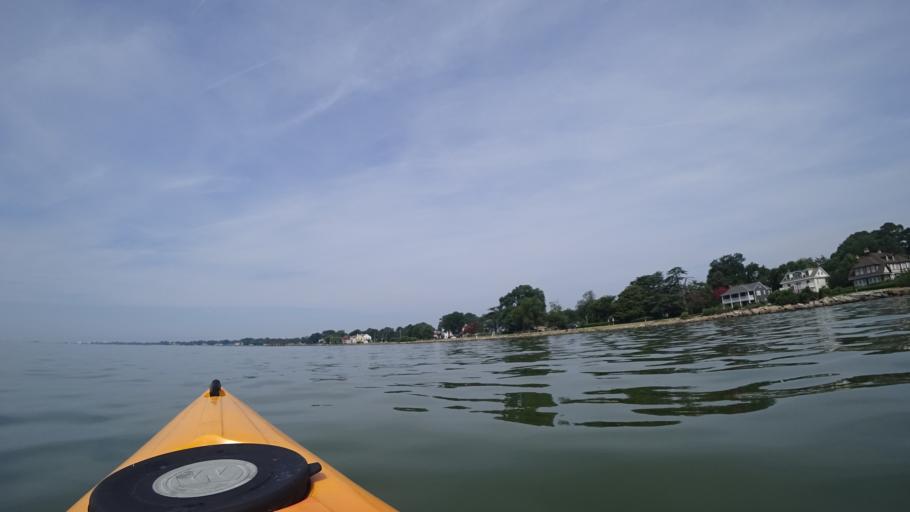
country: US
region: Virginia
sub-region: City of Hampton
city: Hampton
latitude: 36.9998
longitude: -76.3671
